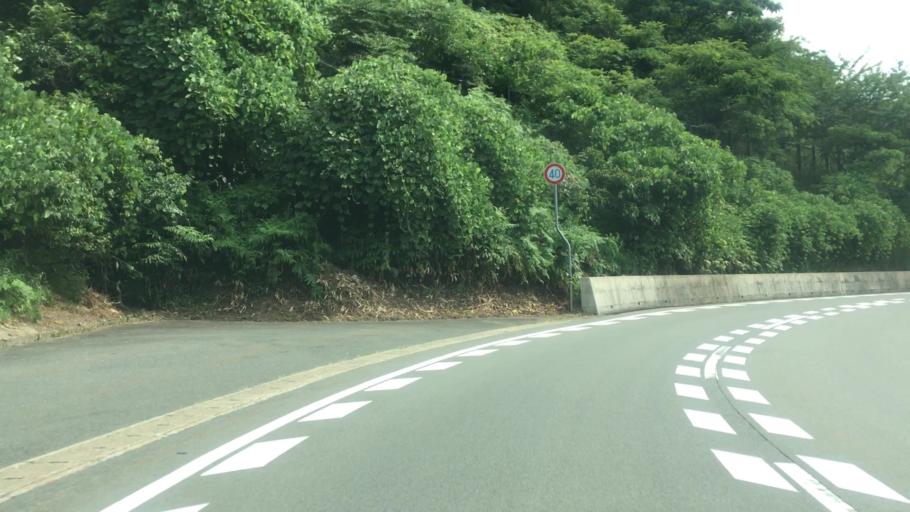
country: JP
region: Hyogo
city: Toyooka
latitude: 35.5228
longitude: 134.7911
